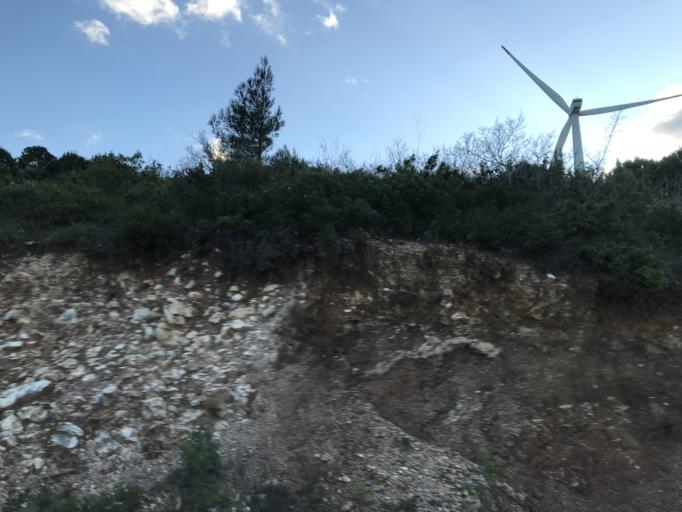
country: TR
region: Hatay
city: Uzunbag
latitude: 36.1065
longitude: 36.0433
